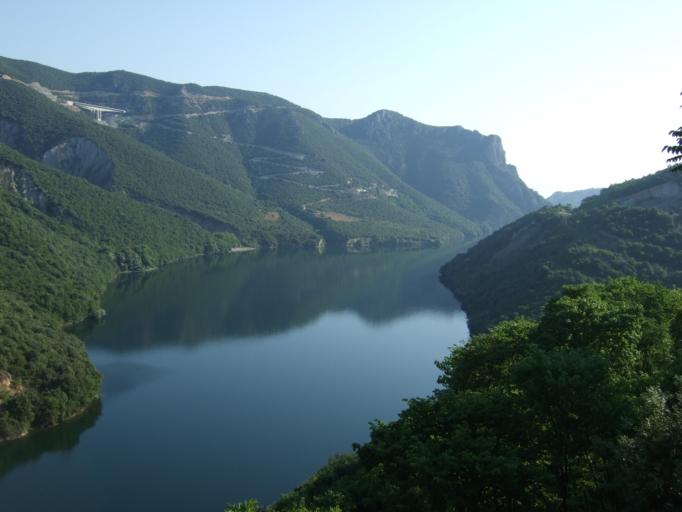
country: GR
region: Central Macedonia
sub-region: Nomos Imathias
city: Veroia
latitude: 40.4422
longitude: 22.2171
